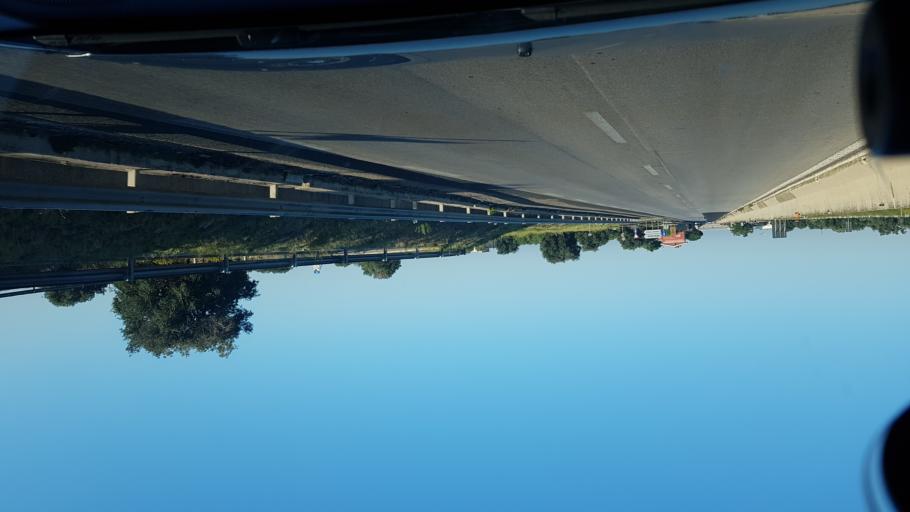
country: IT
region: Apulia
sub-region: Provincia di Brindisi
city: Fasano
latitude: 40.8733
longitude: 17.3420
